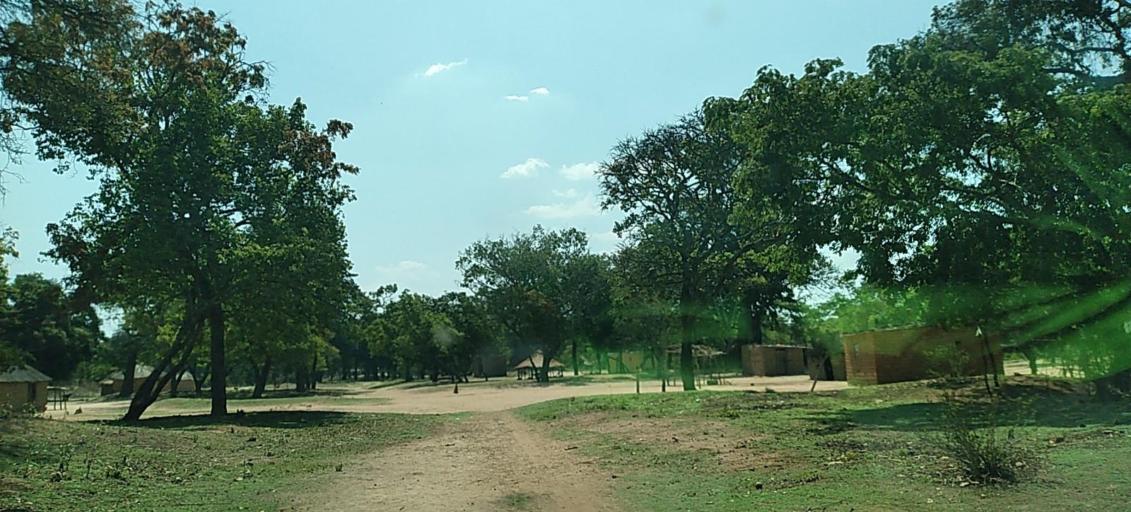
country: CD
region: Katanga
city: Kolwezi
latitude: -11.2753
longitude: 25.1091
